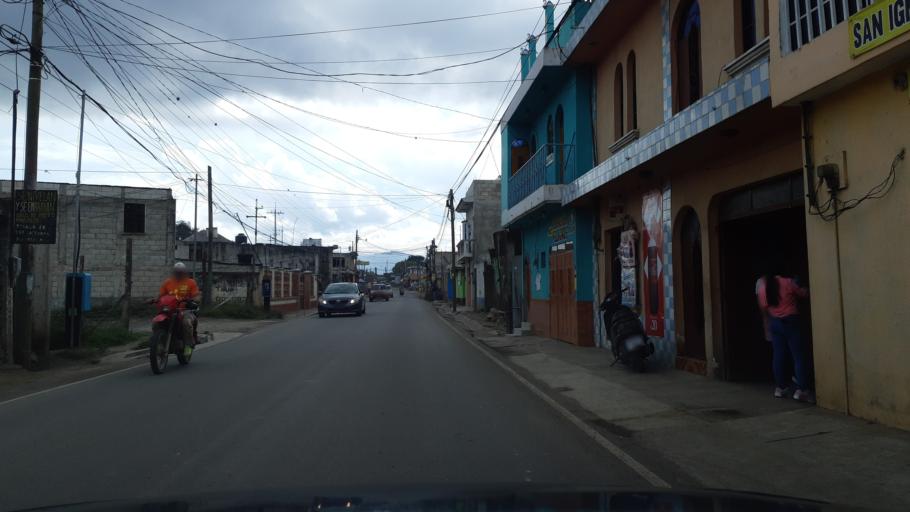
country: GT
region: Chimaltenango
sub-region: Municipio de Chimaltenango
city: Chimaltenango
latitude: 14.6843
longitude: -90.7970
